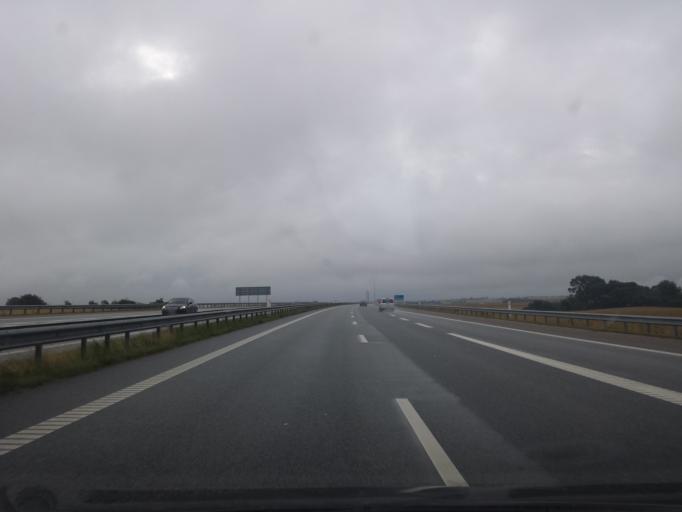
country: DK
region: South Denmark
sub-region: Sonderborg Kommune
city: Dybbol
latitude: 54.9332
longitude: 9.7003
